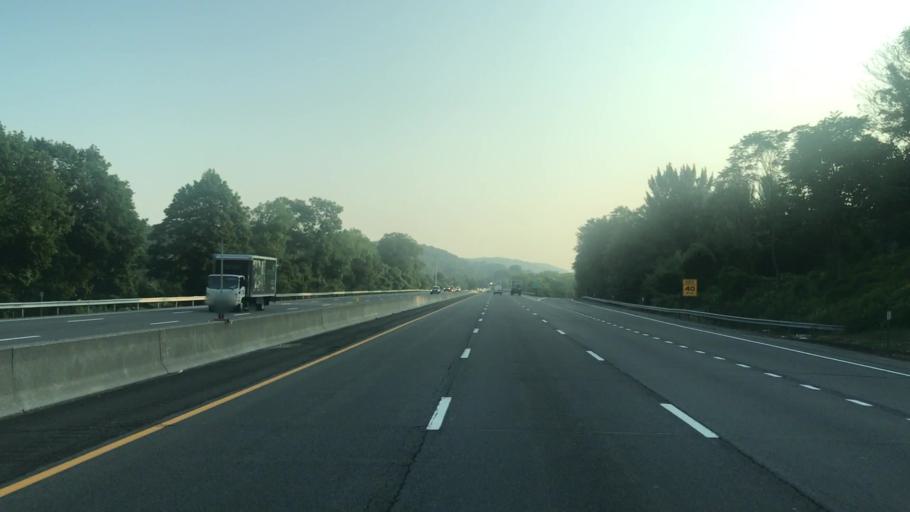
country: US
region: New York
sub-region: Westchester County
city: Ardsley
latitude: 41.0051
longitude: -73.8519
